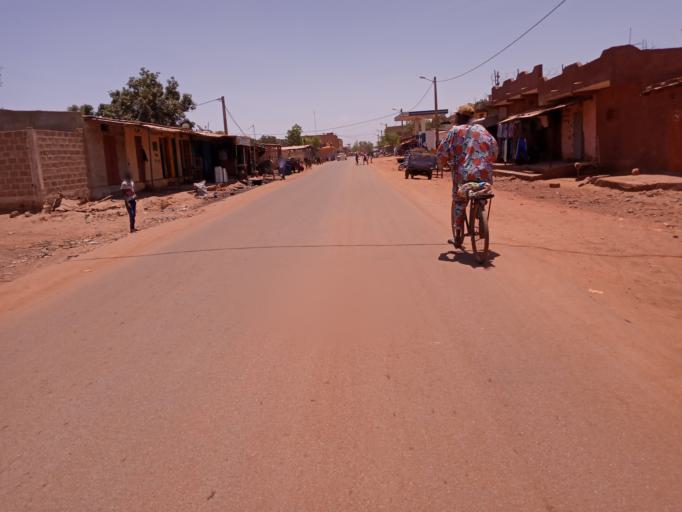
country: ML
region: Bamako
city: Bamako
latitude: 12.5763
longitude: -7.9706
